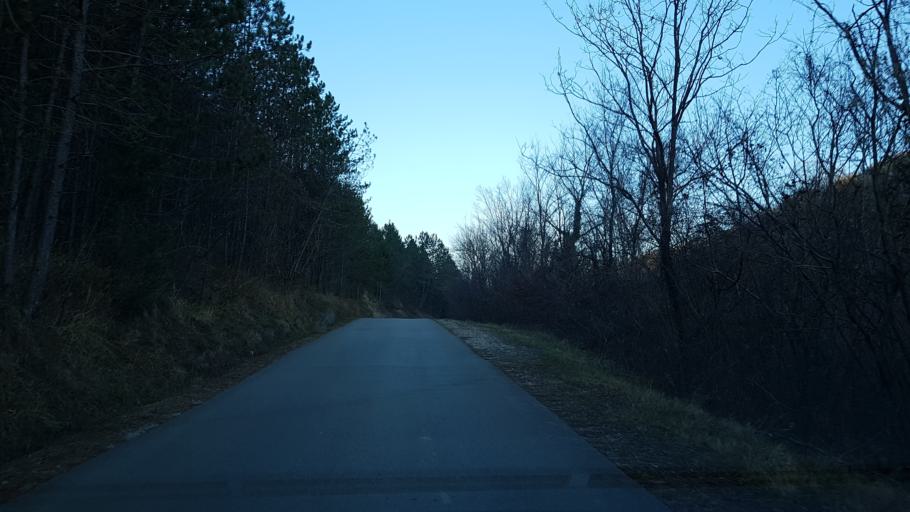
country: SI
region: Koper-Capodistria
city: Prade
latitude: 45.4901
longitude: 13.7746
